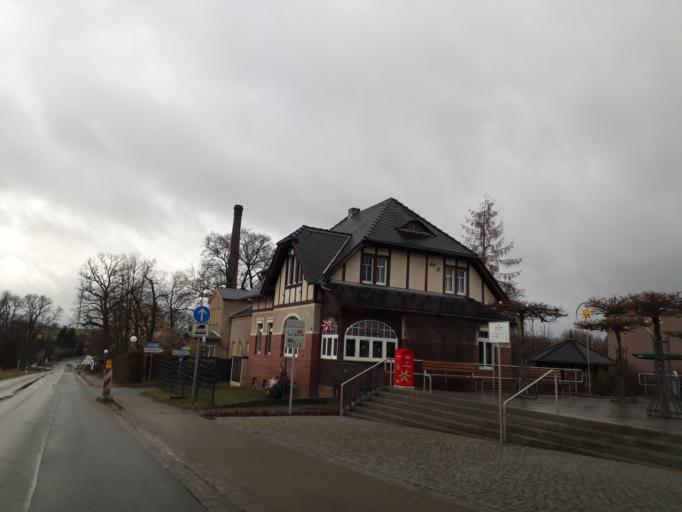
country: DE
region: Saxony
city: Herrnhut
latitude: 51.0161
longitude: 14.7385
